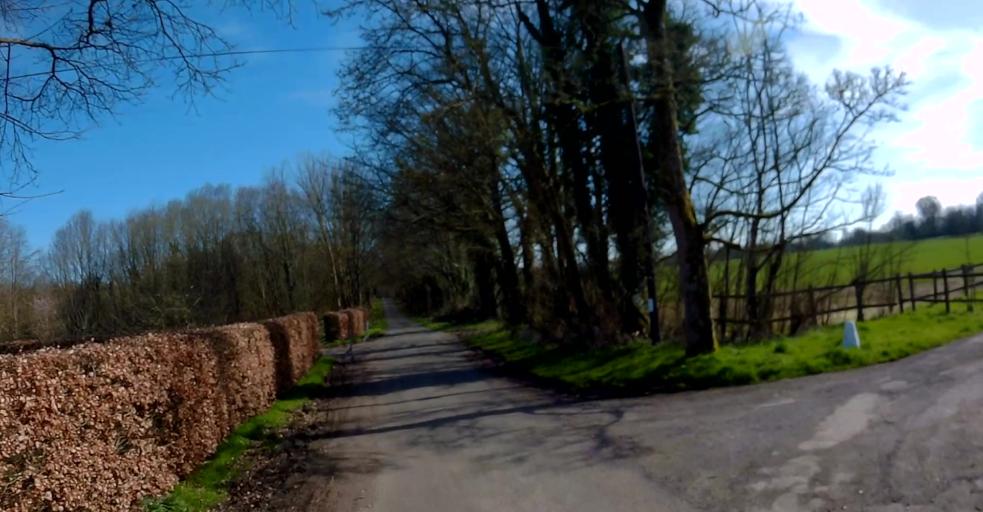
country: GB
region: England
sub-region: Hampshire
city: Four Marks
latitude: 51.1807
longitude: -1.0686
